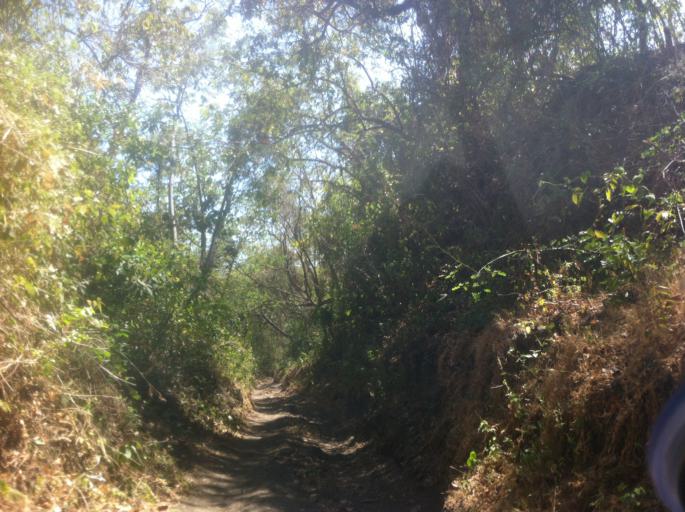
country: NI
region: Chinandega
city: Chichigalpa
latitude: 12.6880
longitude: -87.0275
